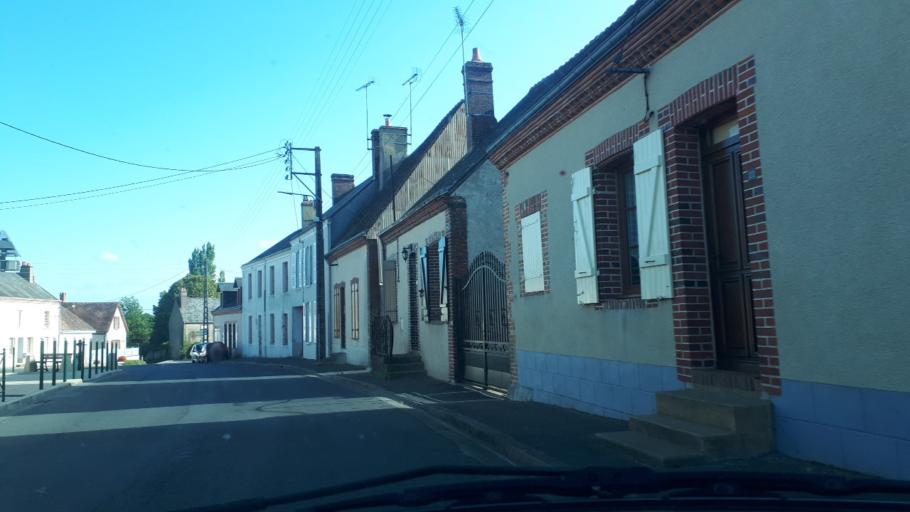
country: FR
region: Centre
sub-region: Departement du Loir-et-Cher
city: Mondoubleau
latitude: 47.9981
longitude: 0.9287
